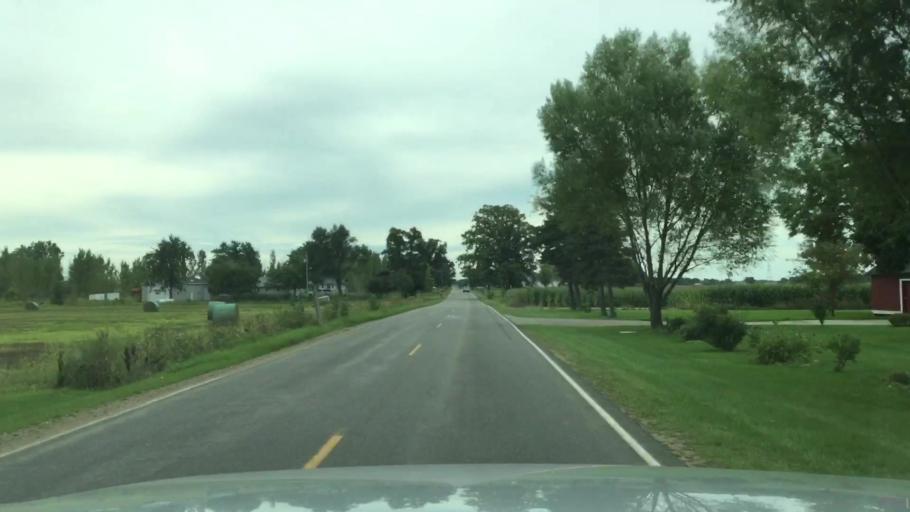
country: US
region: Michigan
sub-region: Shiawassee County
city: Durand
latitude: 43.0155
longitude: -83.9871
